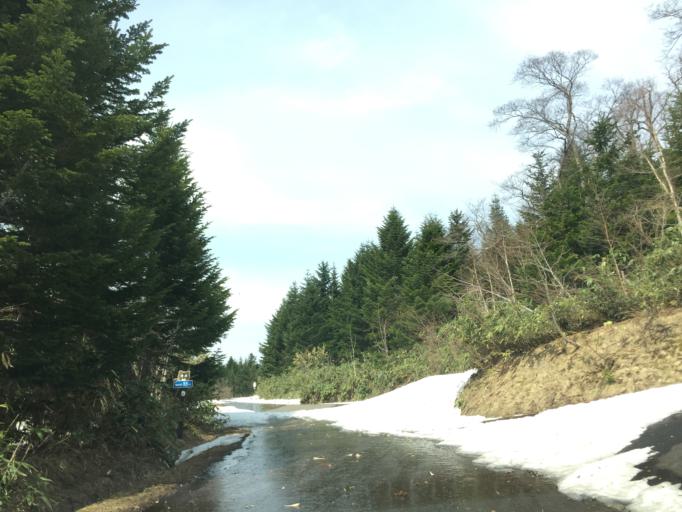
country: JP
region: Hokkaido
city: Akabira
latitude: 43.6073
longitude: 142.0684
